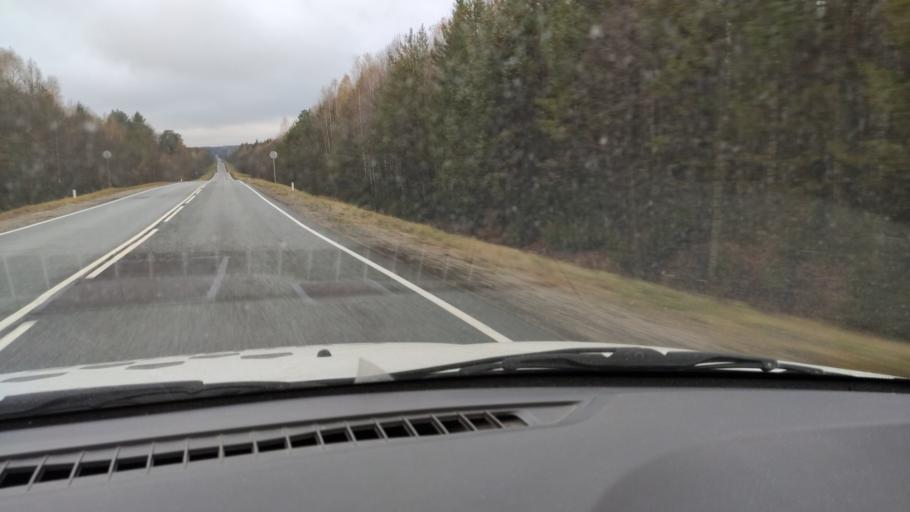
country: RU
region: Kirov
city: Dubrovka
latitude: 58.8998
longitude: 51.3041
